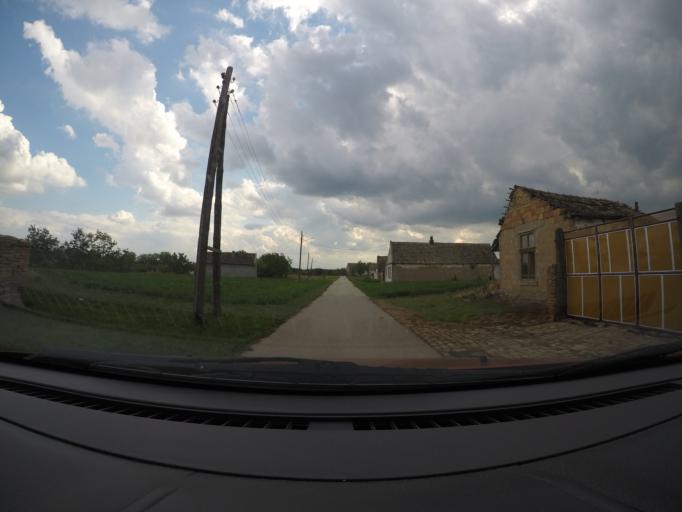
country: RS
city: Uzdin
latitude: 45.2049
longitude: 20.6122
